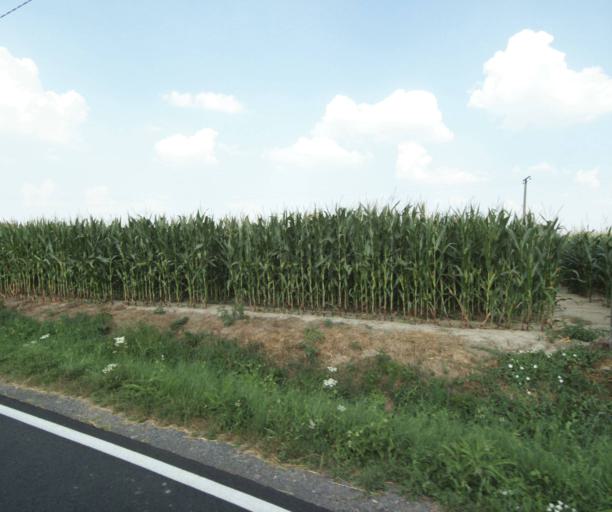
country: FR
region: Nord-Pas-de-Calais
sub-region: Departement du Nord
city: Linselles
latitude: 50.7228
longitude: 3.0609
